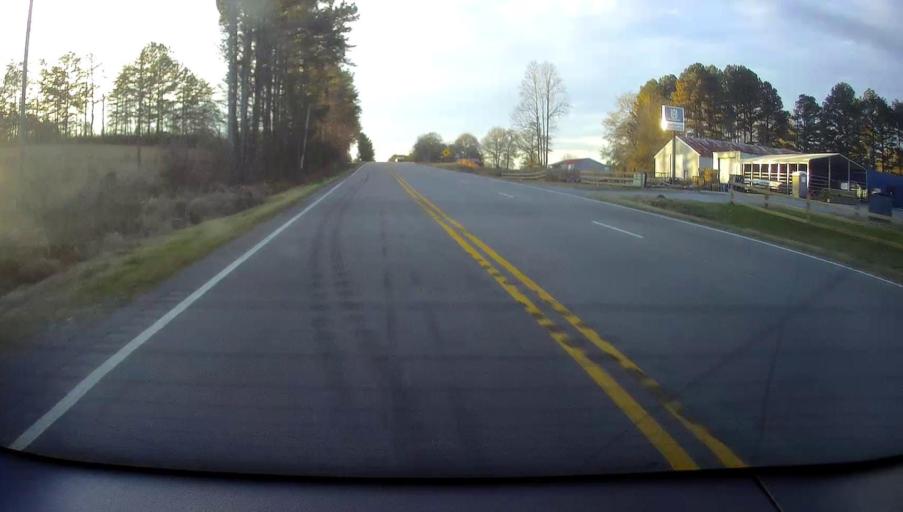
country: US
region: Alabama
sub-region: Etowah County
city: Attalla
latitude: 34.0511
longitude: -86.1842
